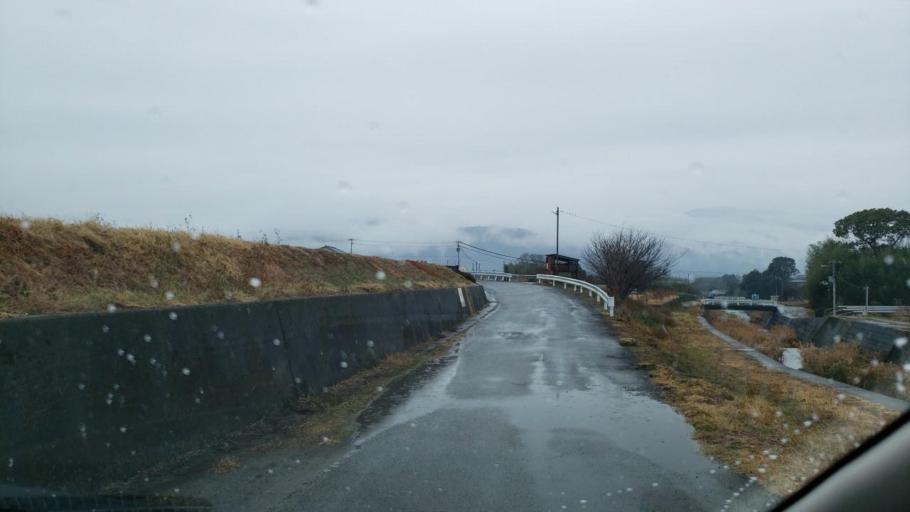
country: JP
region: Tokushima
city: Kamojimacho-jogejima
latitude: 34.0837
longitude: 134.2563
